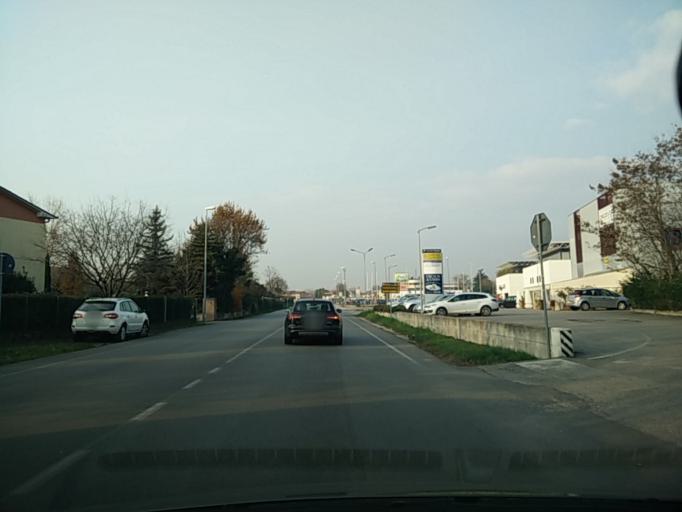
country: IT
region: Veneto
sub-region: Provincia di Treviso
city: Salvatronda
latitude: 45.6810
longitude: 11.9575
